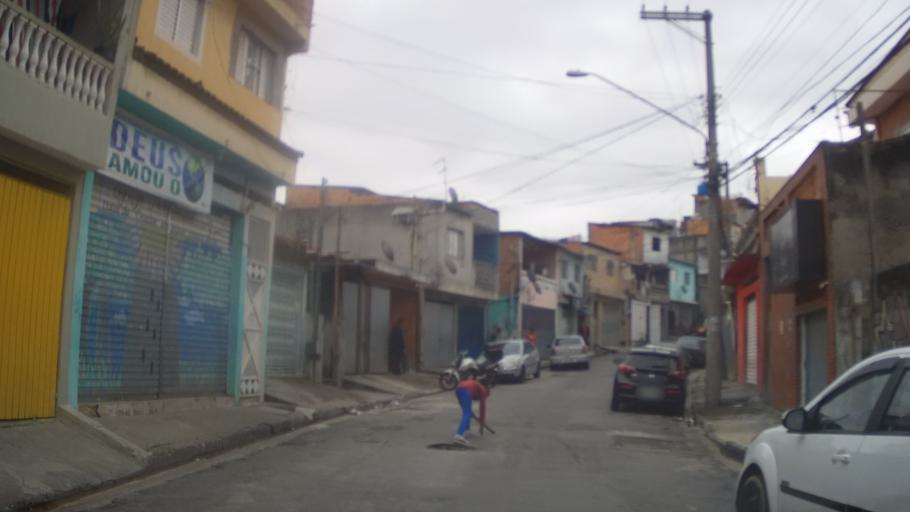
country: BR
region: Sao Paulo
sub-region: Guarulhos
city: Guarulhos
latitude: -23.4487
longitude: -46.5423
